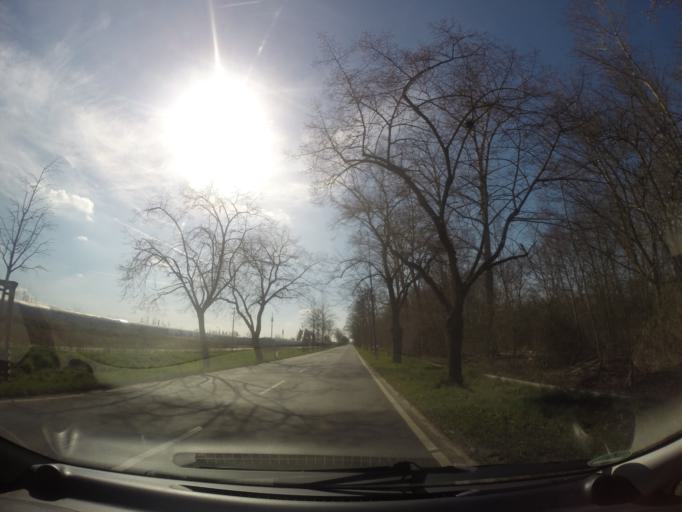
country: DE
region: Berlin
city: Falkenberg
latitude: 52.5604
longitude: 13.5338
